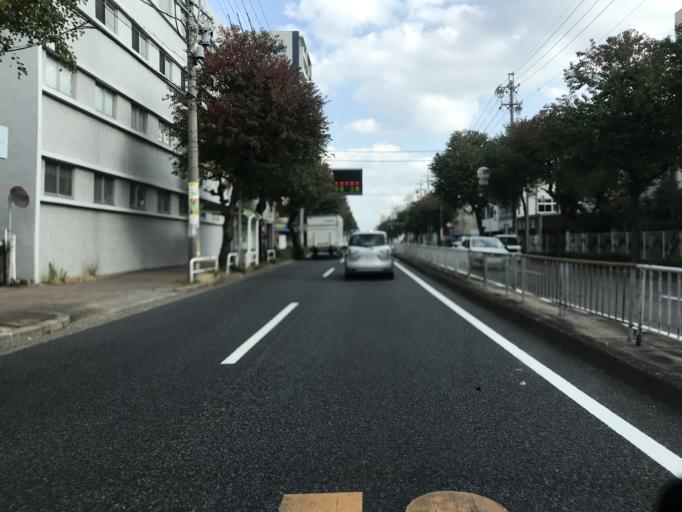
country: JP
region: Aichi
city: Nagoya-shi
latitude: 35.1777
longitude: 136.8618
